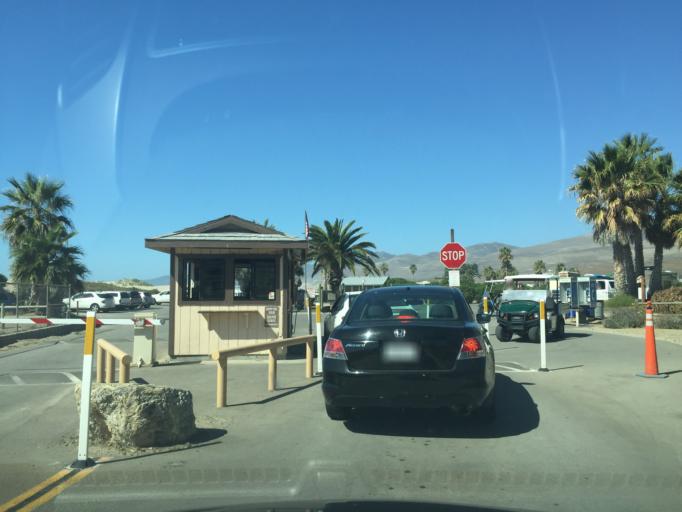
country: US
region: California
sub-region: Santa Barbara County
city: Lompoc
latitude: 34.5096
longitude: -120.5006
